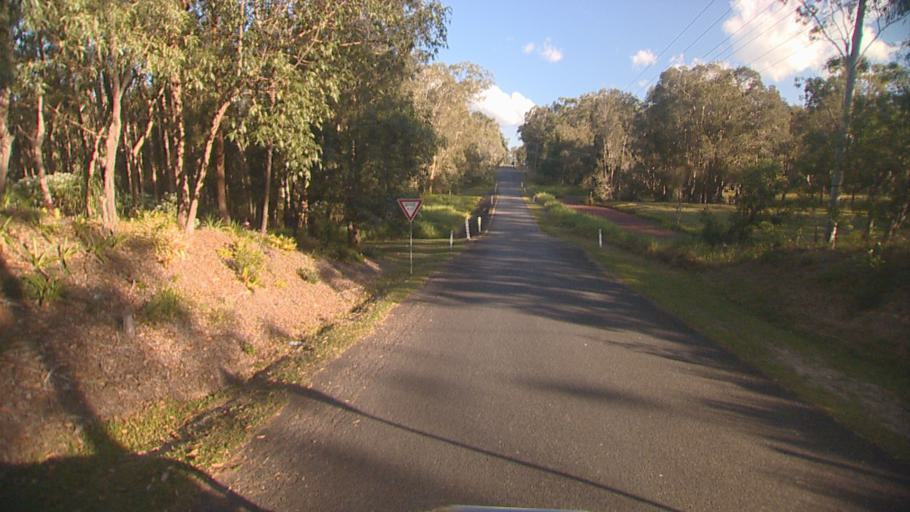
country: AU
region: Queensland
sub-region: Gold Coast
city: Yatala
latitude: -27.6688
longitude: 153.2444
